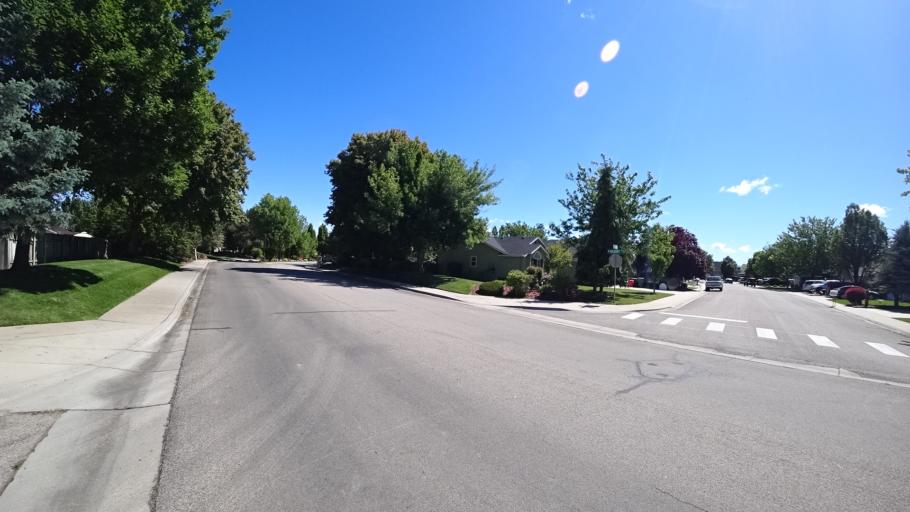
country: US
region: Idaho
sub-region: Ada County
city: Meridian
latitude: 43.6227
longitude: -116.3647
